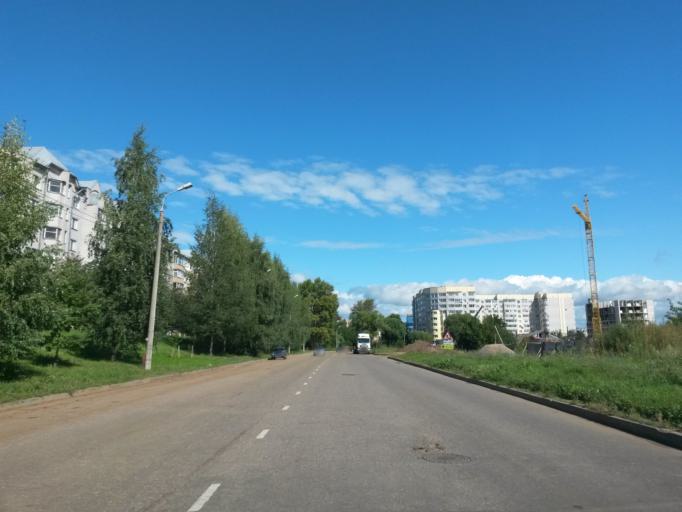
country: RU
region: Jaroslavl
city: Yaroslavl
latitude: 57.5858
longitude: 39.8657
